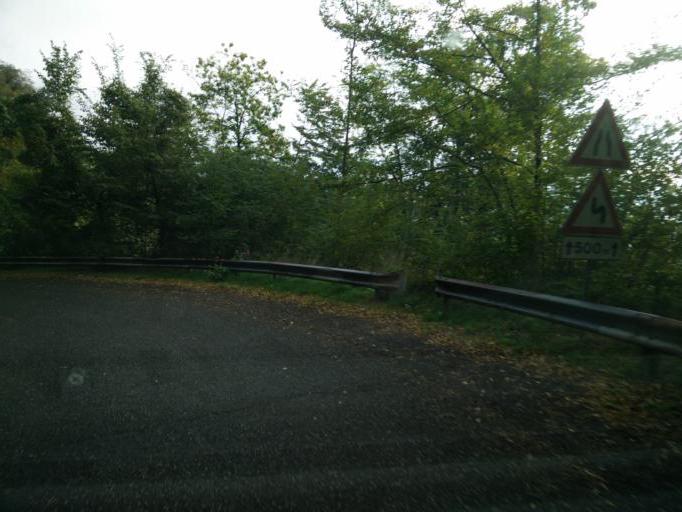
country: IT
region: Tuscany
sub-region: Provincia di Massa-Carrara
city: Pontremoli
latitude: 44.3690
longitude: 9.8290
